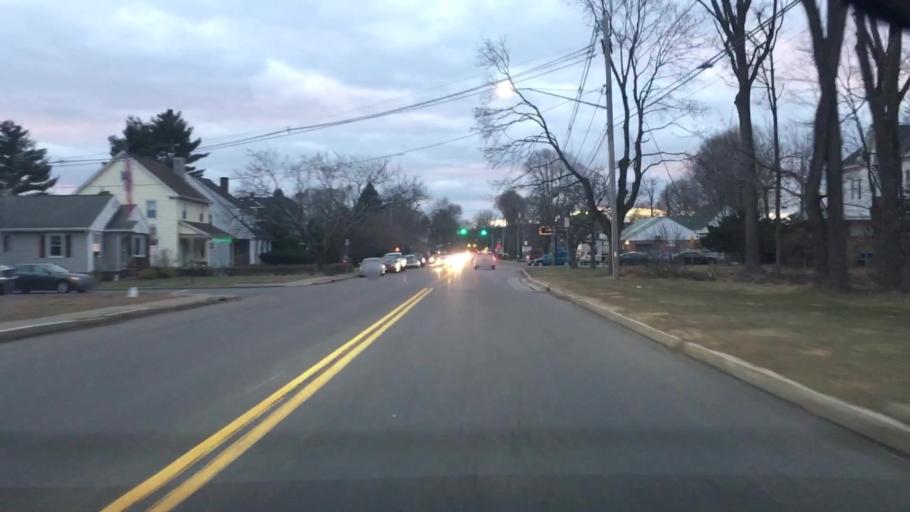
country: US
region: New York
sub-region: Dutchess County
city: Arlington
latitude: 41.6845
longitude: -73.9056
